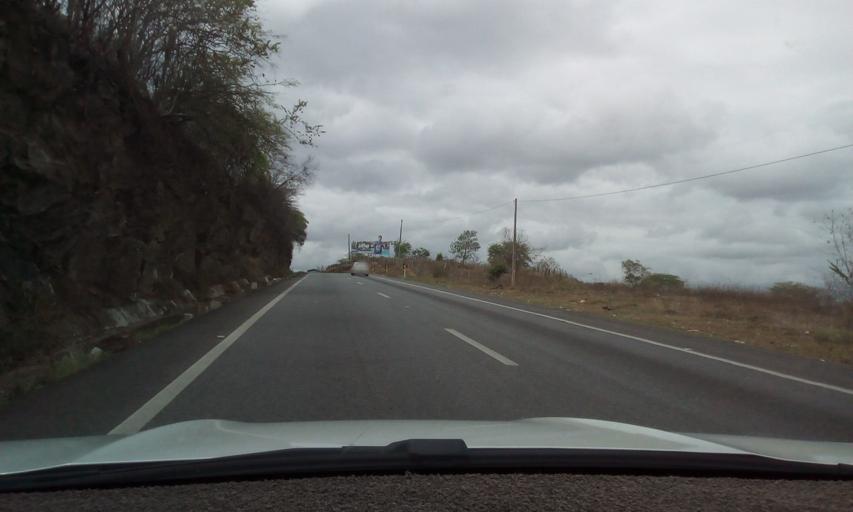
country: BR
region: Paraiba
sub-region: Inga
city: Inga
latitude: -7.2521
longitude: -35.6863
